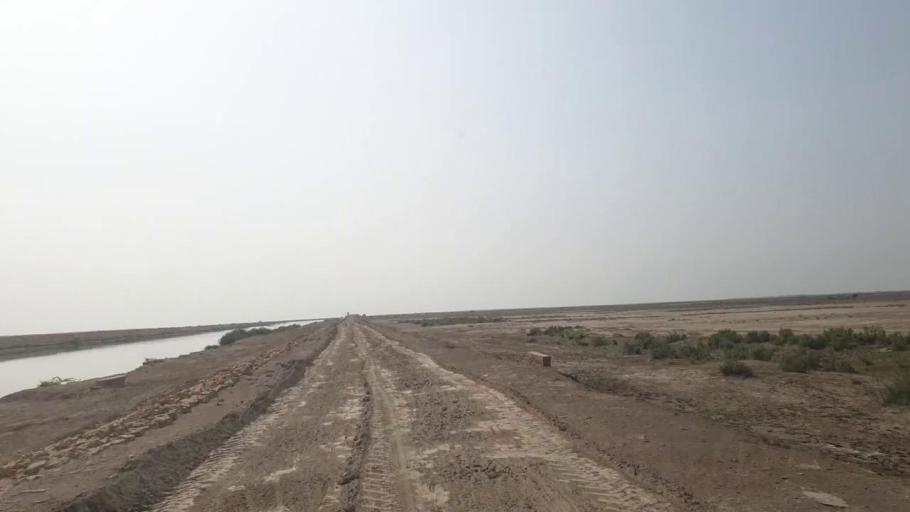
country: PK
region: Sindh
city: Kadhan
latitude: 24.3307
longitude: 68.8344
